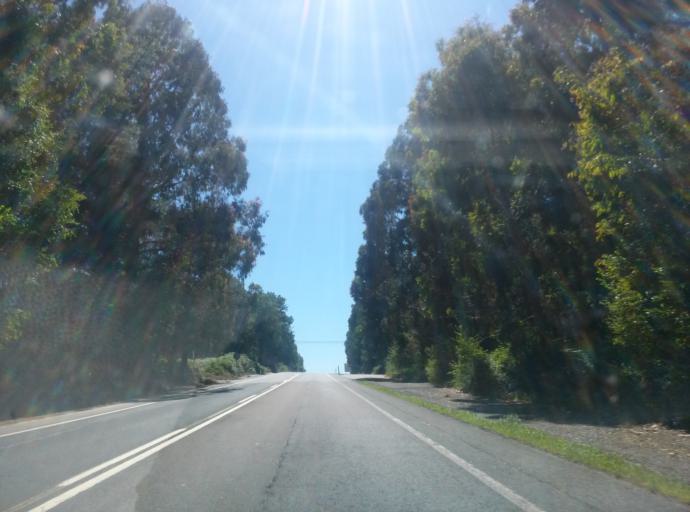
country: ES
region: Galicia
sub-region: Provincia de Lugo
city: Mos
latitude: 43.1019
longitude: -7.4691
